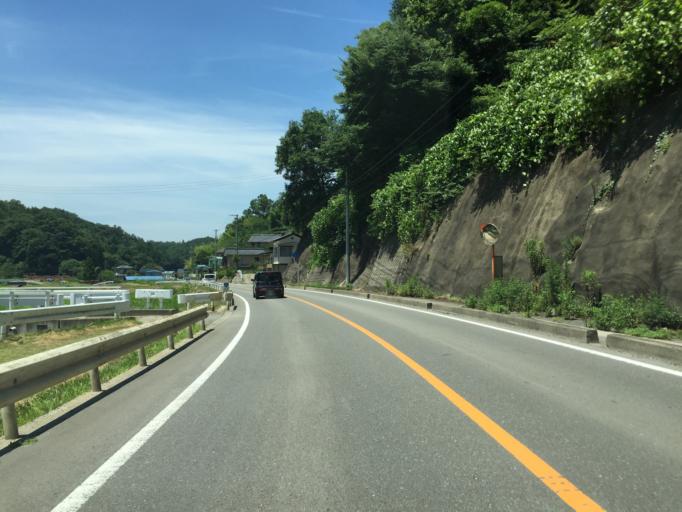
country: JP
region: Fukushima
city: Hobaramachi
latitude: 37.7634
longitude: 140.6210
